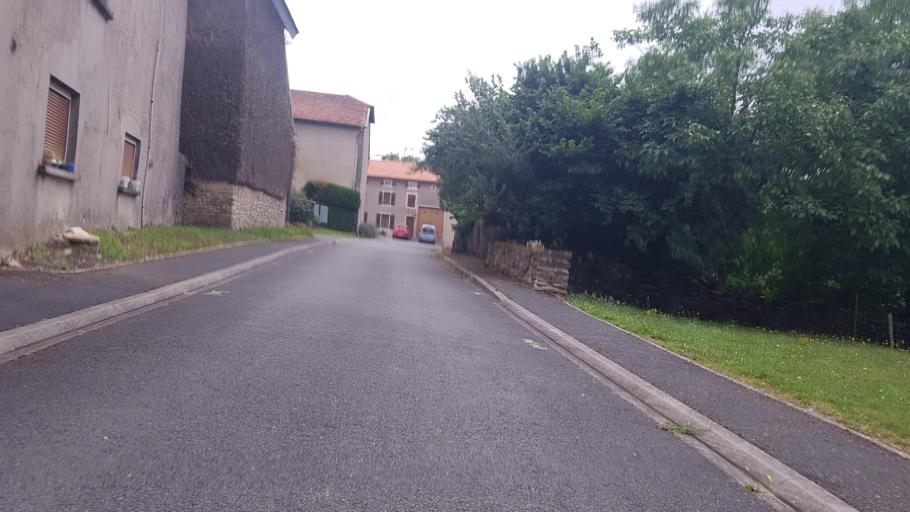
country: FR
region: Lorraine
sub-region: Departement de la Moselle
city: Lorquin
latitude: 48.6970
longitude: 6.9954
